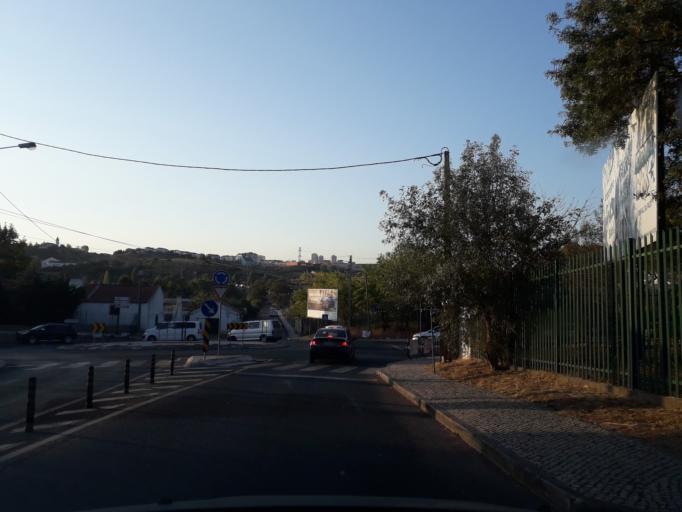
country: PT
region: Lisbon
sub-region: Odivelas
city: Pontinha
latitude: 38.7765
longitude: -9.2057
